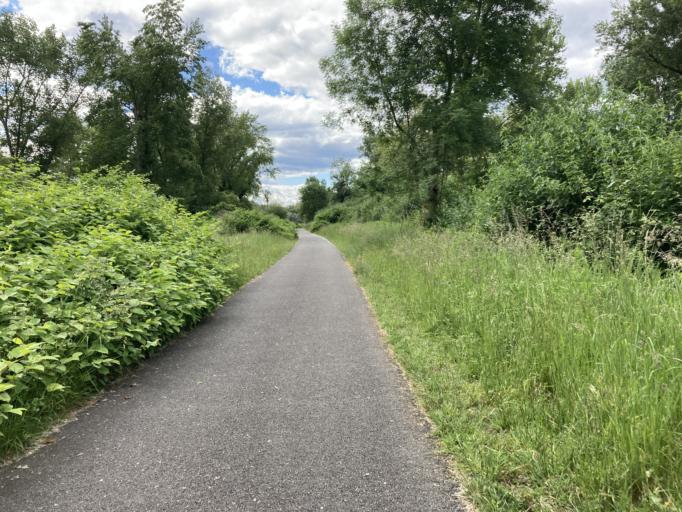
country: FR
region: Aquitaine
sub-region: Departement des Pyrenees-Atlantiques
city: Artiguelouve
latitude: 43.3237
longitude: -0.4570
